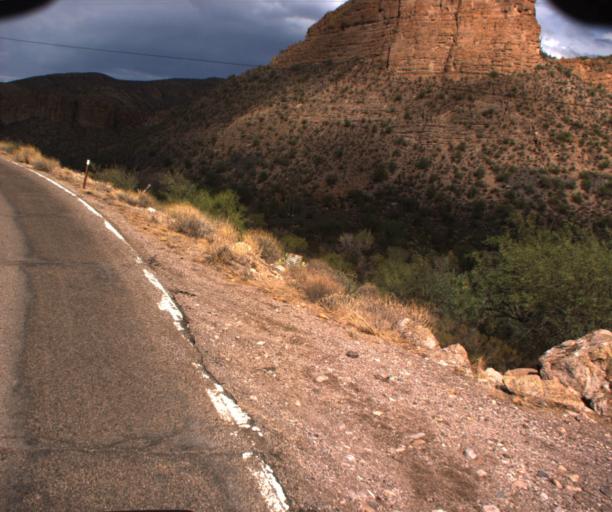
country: US
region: Arizona
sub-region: Pinal County
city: Apache Junction
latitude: 33.5260
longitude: -111.3924
